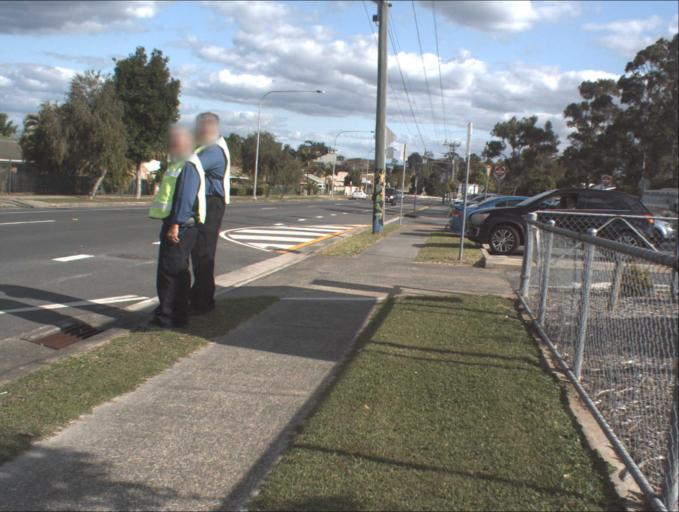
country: AU
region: Queensland
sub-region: Logan
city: Logan Reserve
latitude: -27.6918
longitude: 153.0828
